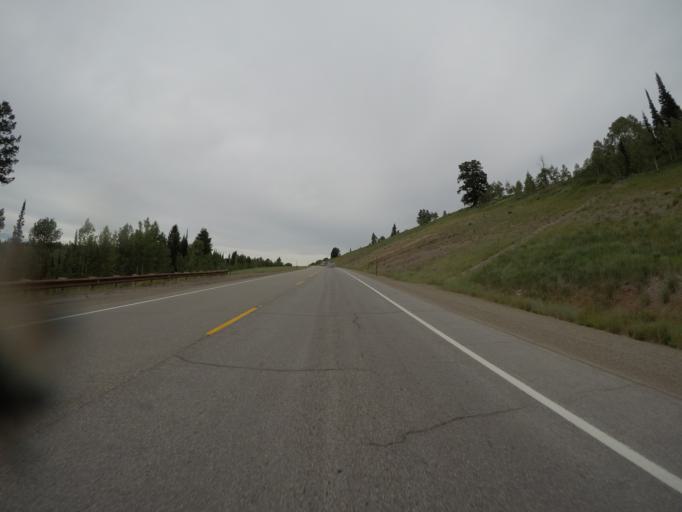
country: US
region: Wyoming
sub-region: Lincoln County
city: Afton
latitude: 42.5002
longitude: -110.9091
